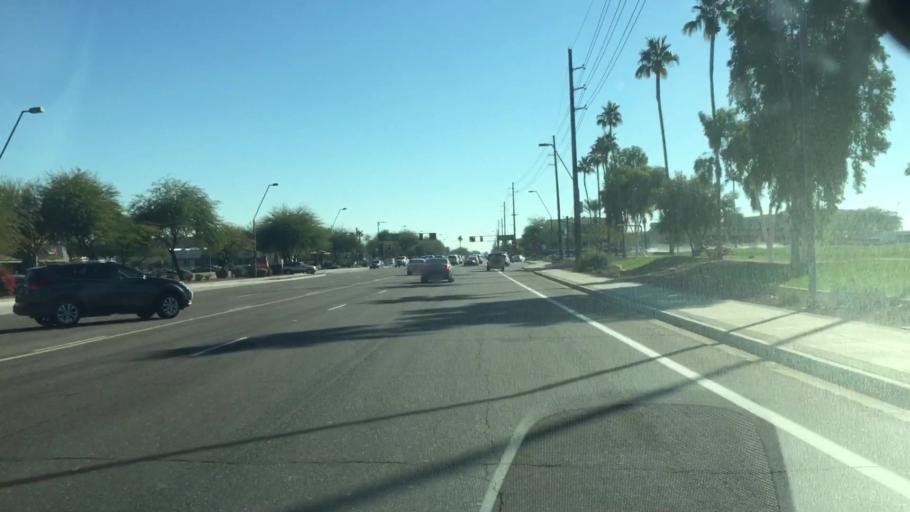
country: US
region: Arizona
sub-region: Maricopa County
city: Guadalupe
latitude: 33.3363
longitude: -111.9632
